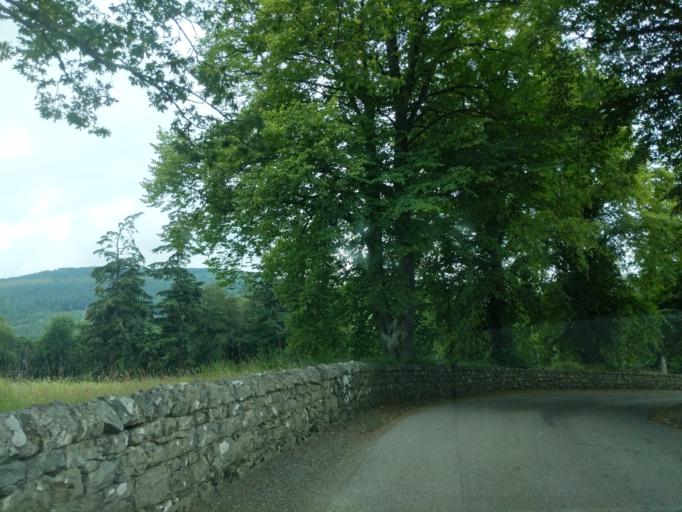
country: GB
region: Scotland
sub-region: Moray
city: Rothes
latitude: 57.4108
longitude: -3.3619
